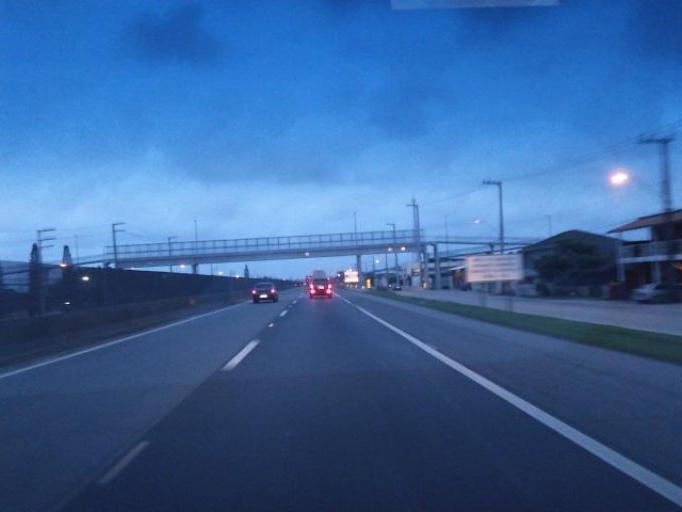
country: BR
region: Santa Catarina
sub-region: Barra Velha
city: Barra Velha
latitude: -26.6618
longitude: -48.6887
